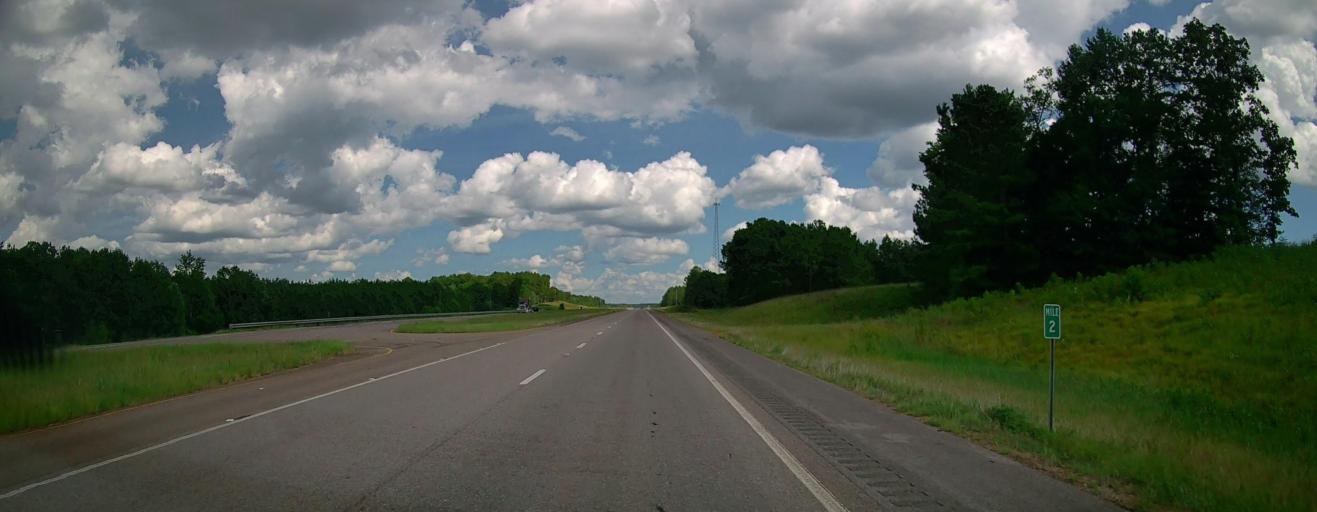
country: US
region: Mississippi
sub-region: Lowndes County
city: New Hope
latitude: 33.4772
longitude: -88.2519
